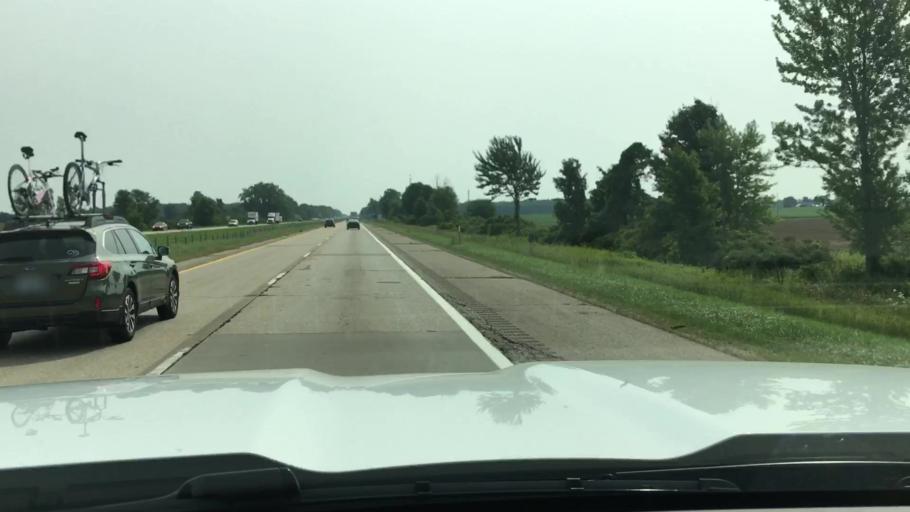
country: US
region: Michigan
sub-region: Ionia County
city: Lake Odessa
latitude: 42.8853
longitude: -85.1207
